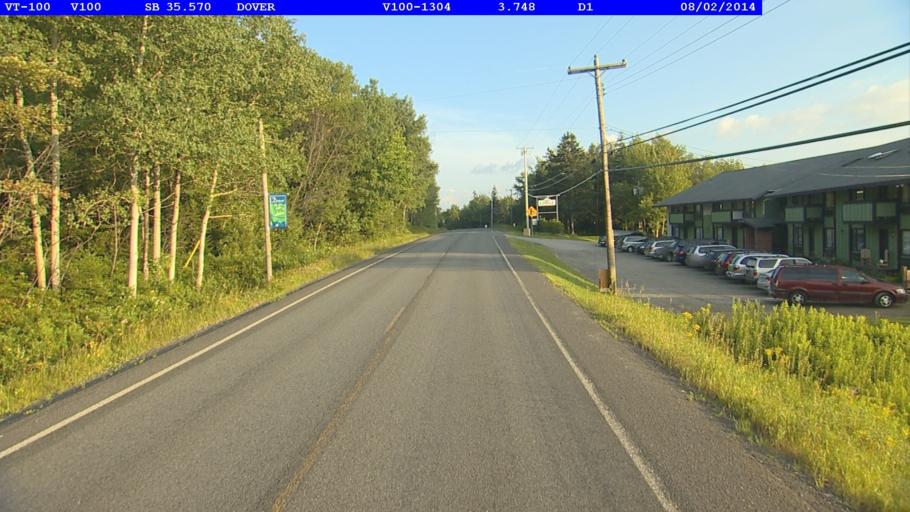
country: US
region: Vermont
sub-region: Windham County
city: Dover
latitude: 42.9652
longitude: -72.8865
